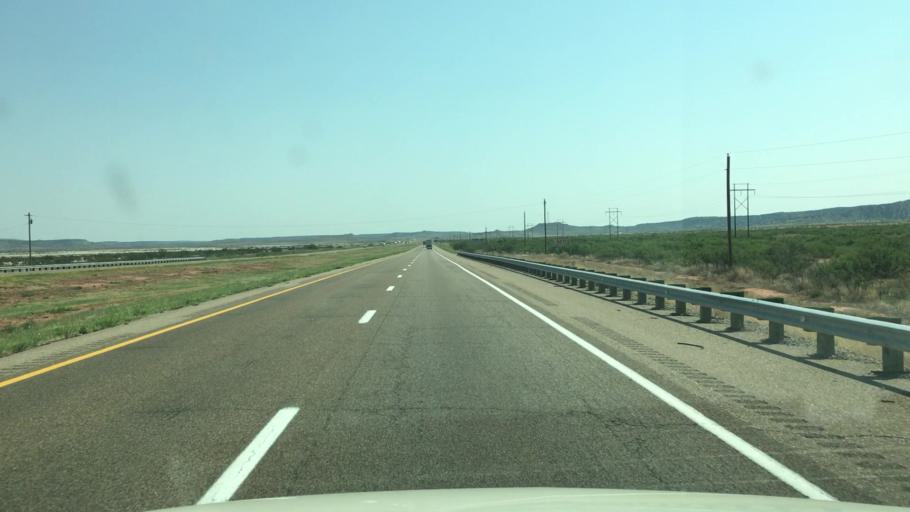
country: US
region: New Mexico
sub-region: Quay County
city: Tucumcari
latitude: 35.1125
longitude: -104.0012
